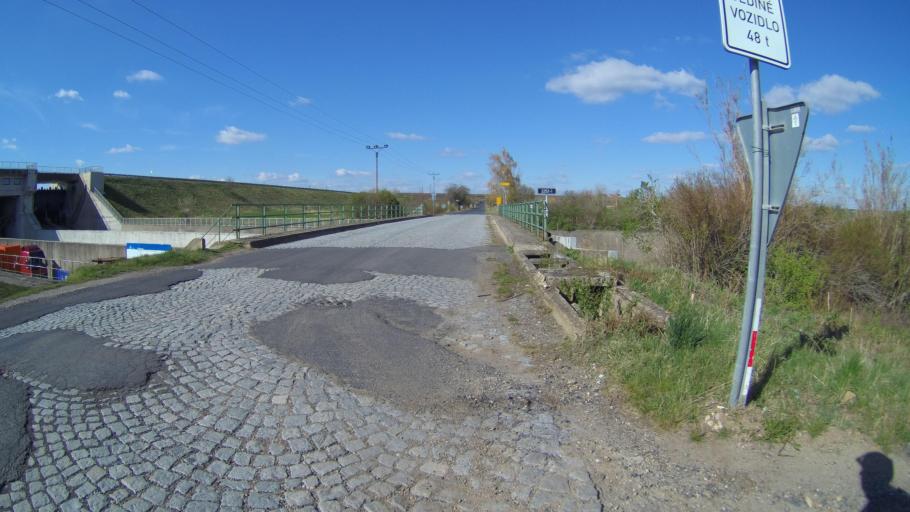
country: CZ
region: Ustecky
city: Brezno
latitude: 50.3703
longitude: 13.4203
